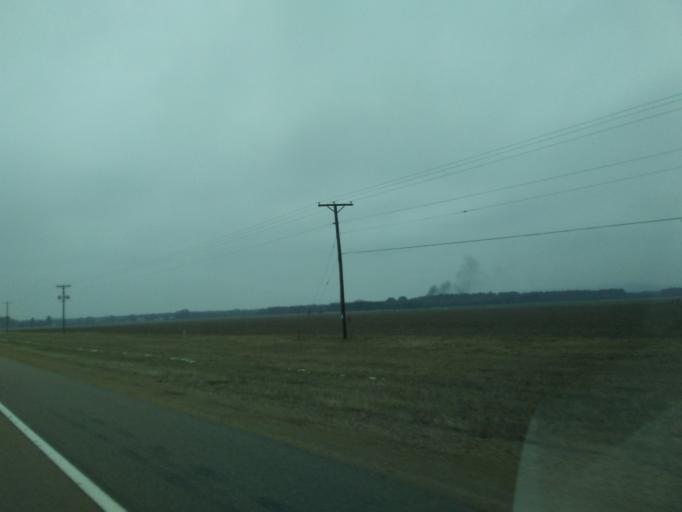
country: US
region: Wisconsin
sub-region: Sauk County
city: Spring Green
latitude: 43.1616
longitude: -90.0061
